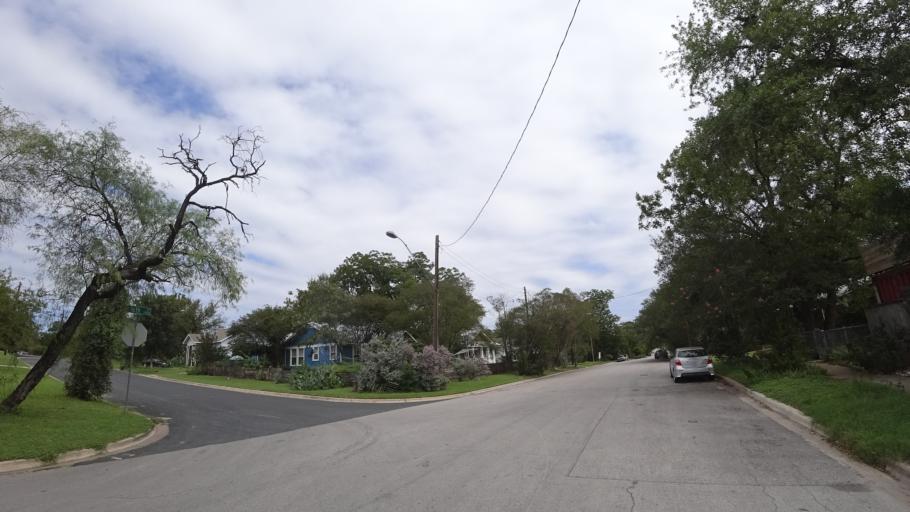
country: US
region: Texas
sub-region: Travis County
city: Austin
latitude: 30.2769
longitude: -97.7194
